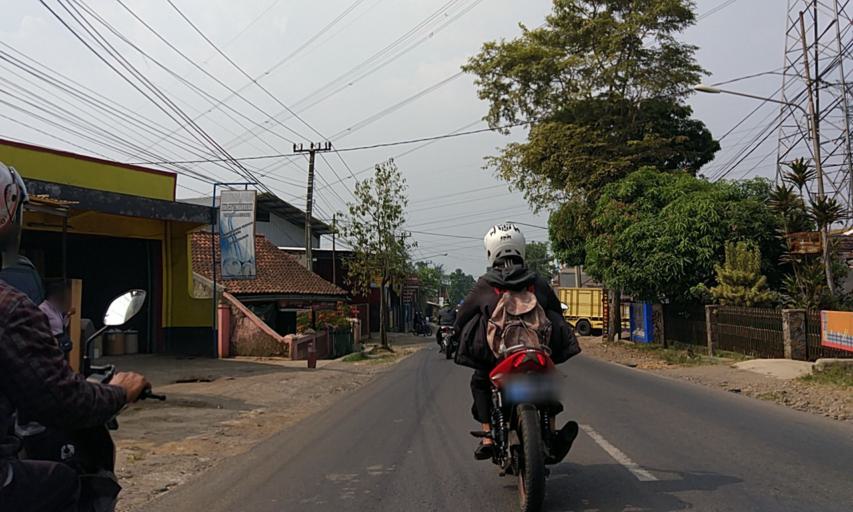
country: ID
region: West Java
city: Banjaran
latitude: -7.0538
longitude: 107.5723
